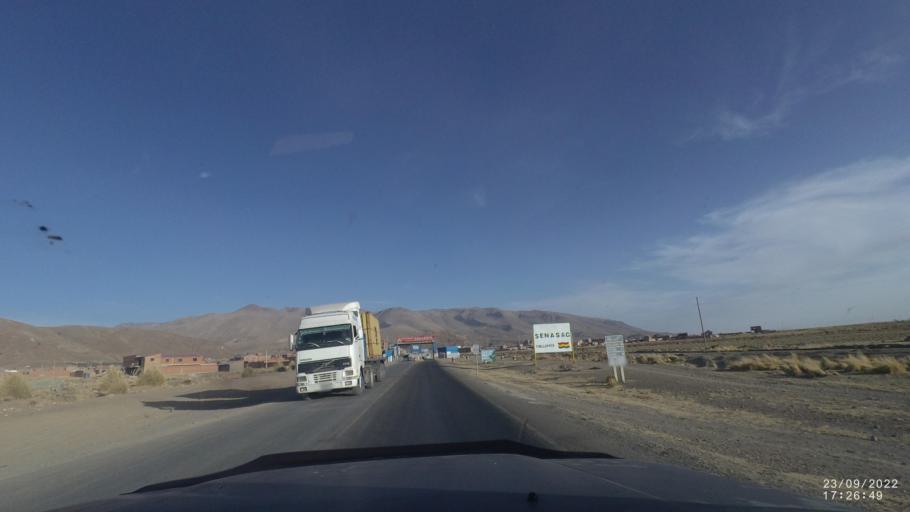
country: BO
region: Oruro
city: Challapata
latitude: -18.8892
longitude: -66.7822
